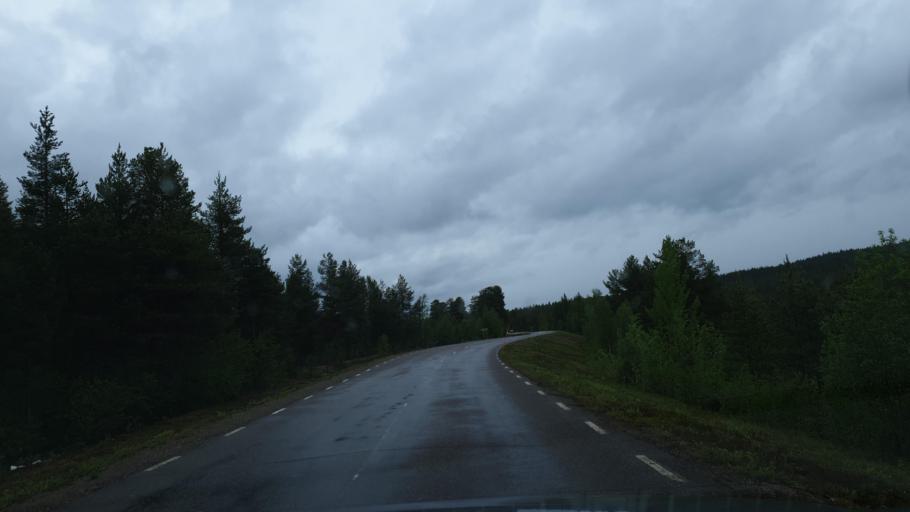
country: SE
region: Norrbotten
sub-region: Kiruna Kommun
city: Kiruna
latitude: 67.8638
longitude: 20.9796
